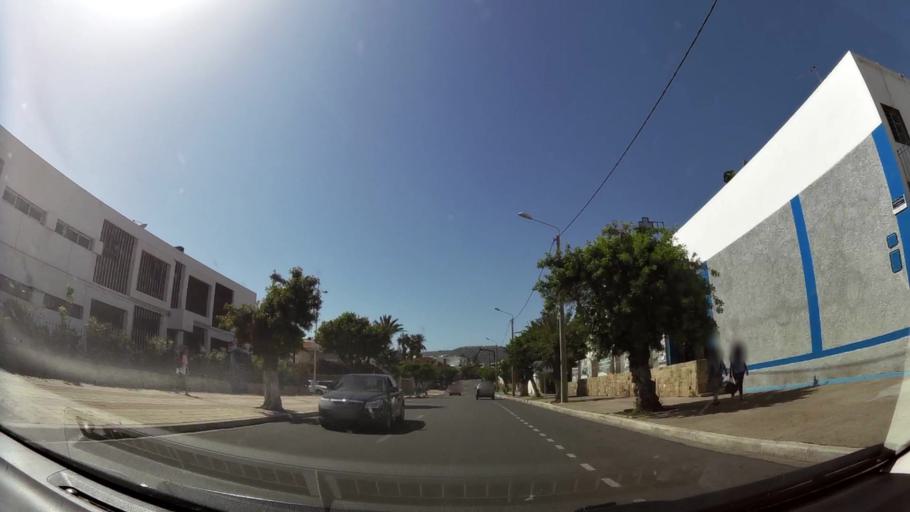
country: MA
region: Souss-Massa-Draa
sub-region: Agadir-Ida-ou-Tnan
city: Agadir
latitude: 30.4258
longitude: -9.6001
